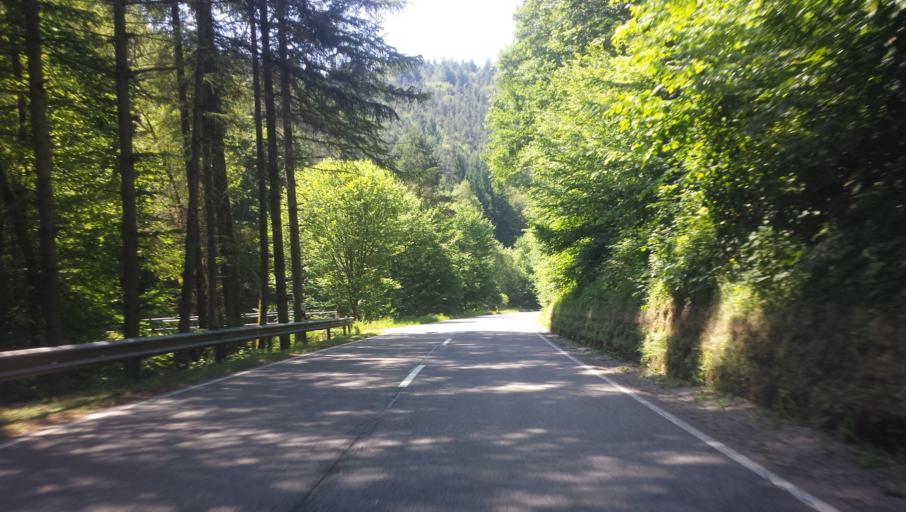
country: DE
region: Rheinland-Pfalz
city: Elmstein
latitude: 49.3583
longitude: 7.8992
